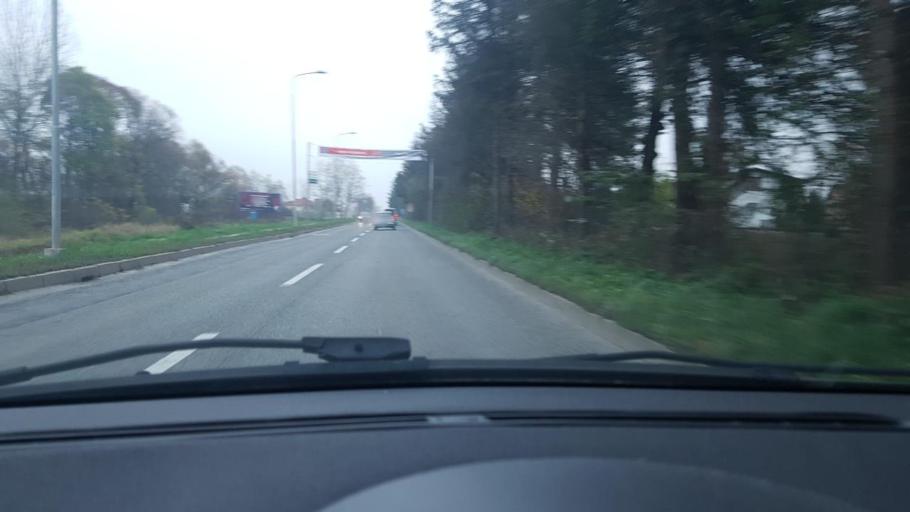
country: SI
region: Celje
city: Celje
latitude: 46.2376
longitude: 15.2390
